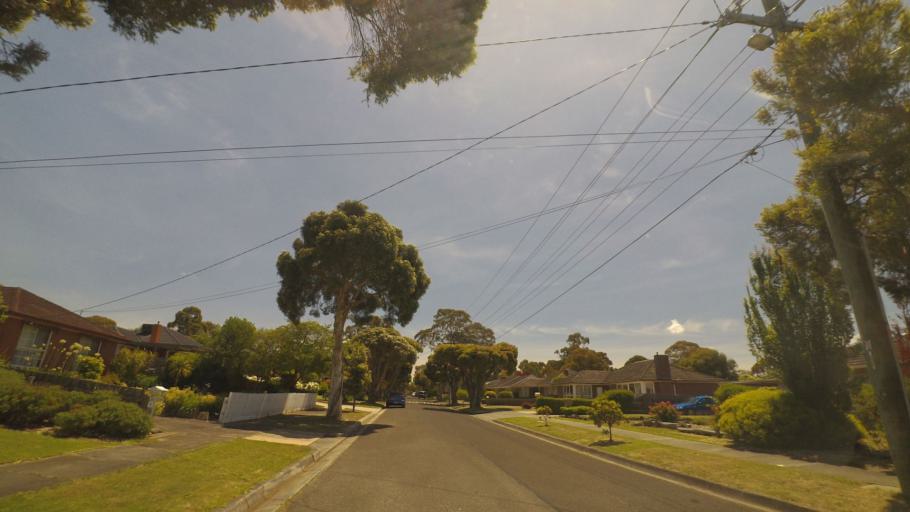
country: AU
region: Victoria
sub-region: Maroondah
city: Bayswater North
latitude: -37.8126
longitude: 145.2964
